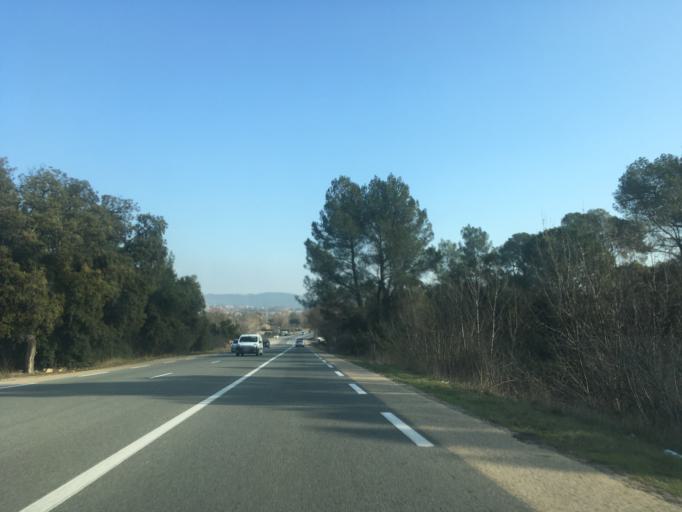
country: FR
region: Provence-Alpes-Cote d'Azur
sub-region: Departement du Var
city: Vidauban
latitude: 43.4368
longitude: 6.4467
